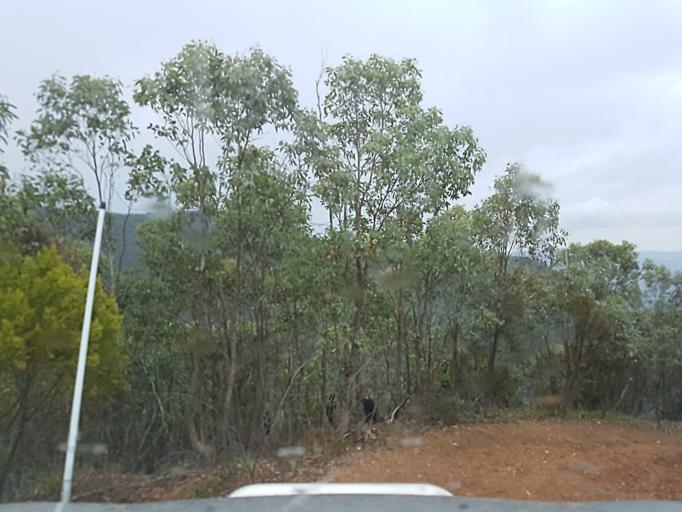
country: AU
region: New South Wales
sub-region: Snowy River
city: Jindabyne
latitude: -36.9237
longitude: 148.3507
